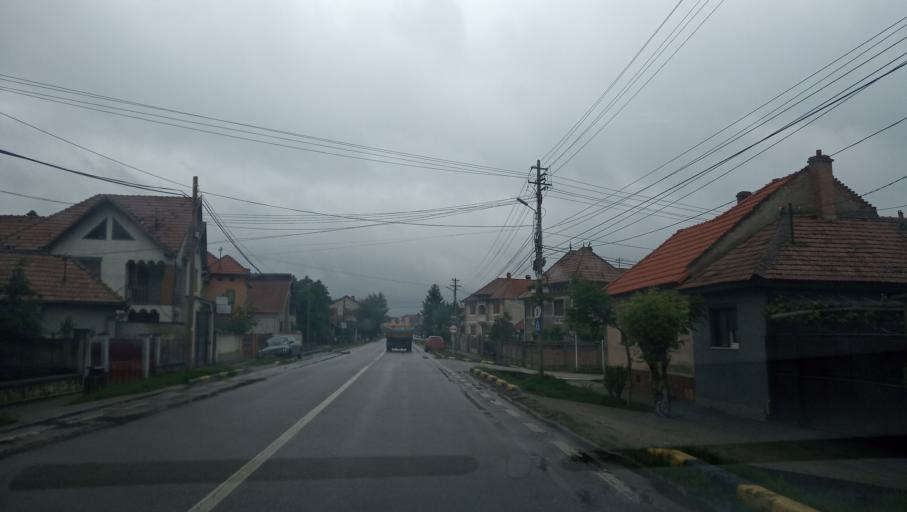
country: RO
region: Alba
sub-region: Municipiul Sebes
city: Sebes
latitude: 45.9513
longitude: 23.5822
